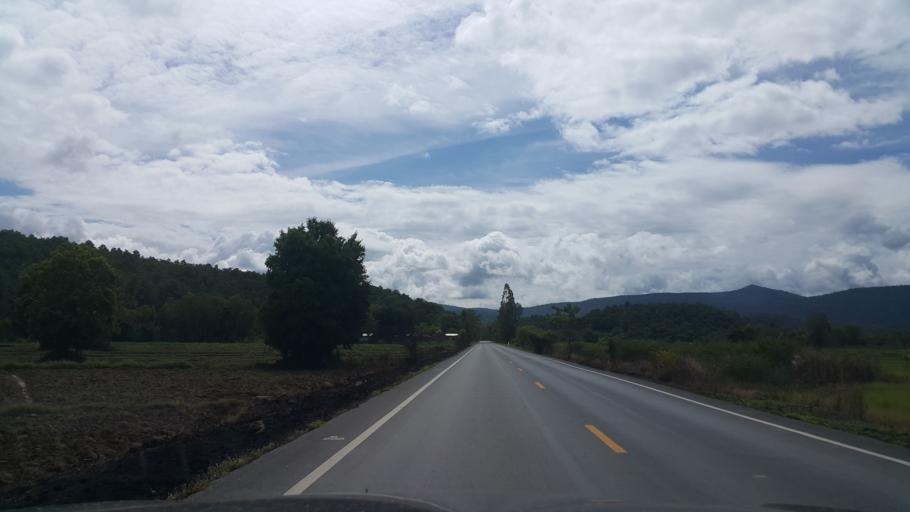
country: TH
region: Uttaradit
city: Thong Saen Khan
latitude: 17.3639
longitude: 100.2398
